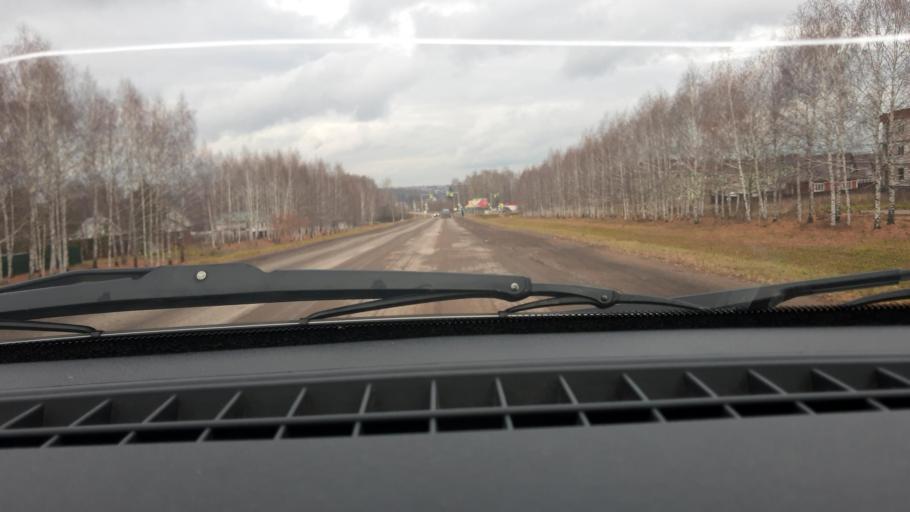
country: RU
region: Bashkortostan
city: Iglino
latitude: 54.8266
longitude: 56.4235
